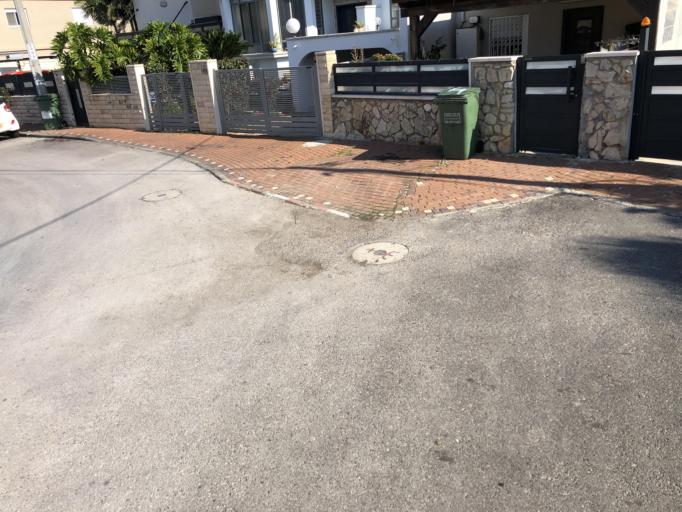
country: IL
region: Northern District
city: `Akko
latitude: 32.9223
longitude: 35.0933
